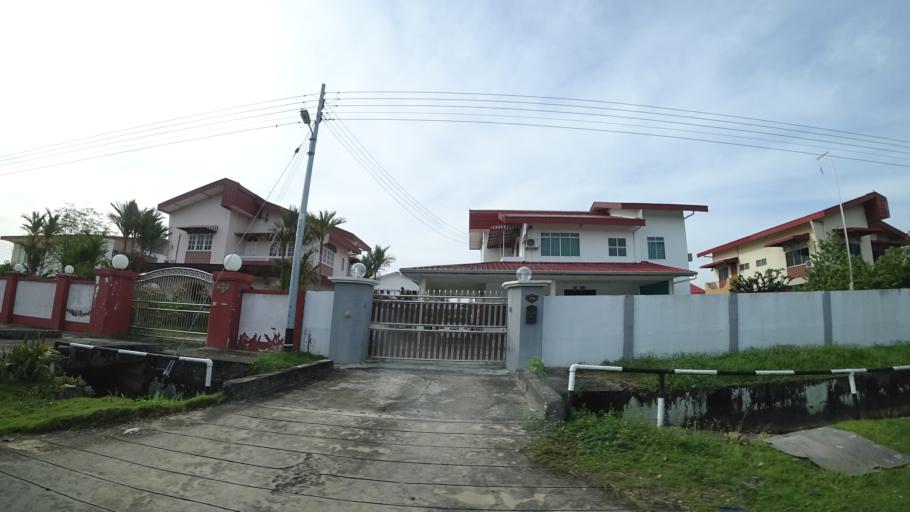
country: MY
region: Sarawak
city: Miri
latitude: 4.4488
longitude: 114.0153
